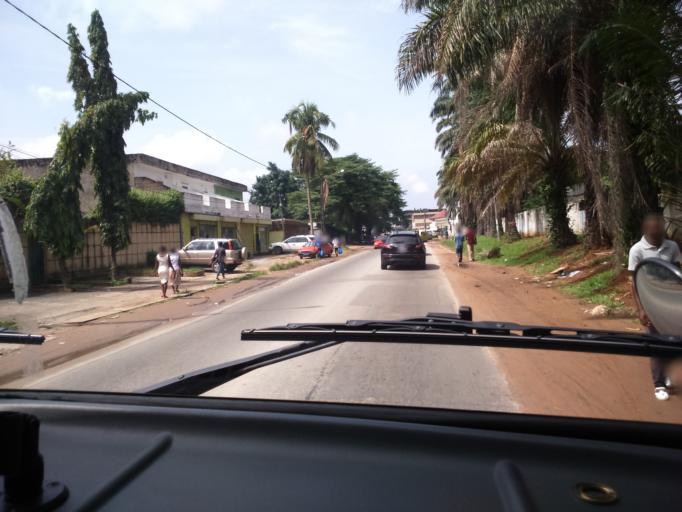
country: CI
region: Lagunes
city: Abidjan
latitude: 5.3585
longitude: -3.9784
